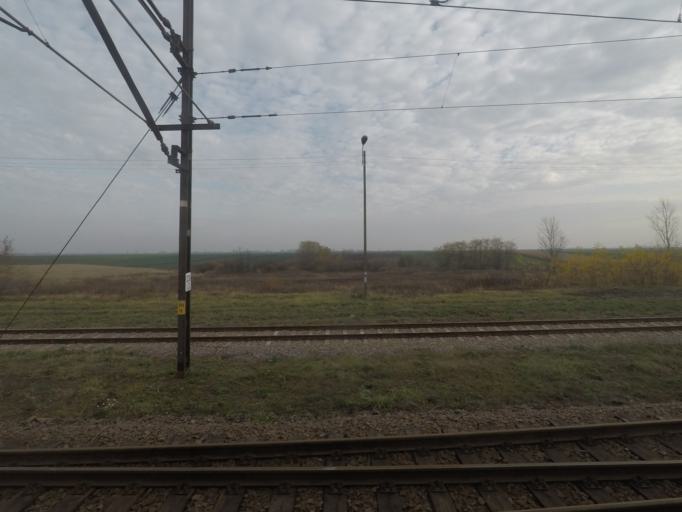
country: PL
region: Subcarpathian Voivodeship
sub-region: Powiat przemyski
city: Orly
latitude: 49.8454
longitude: 22.8475
